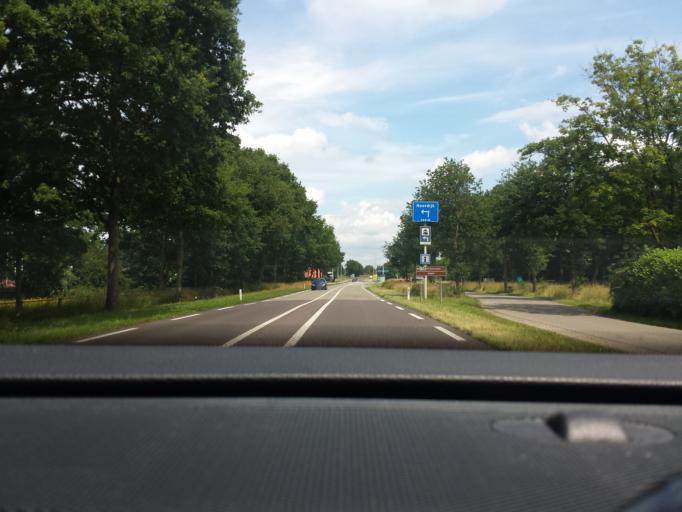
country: NL
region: Gelderland
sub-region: Berkelland
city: Neede
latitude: 52.1328
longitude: 6.5910
